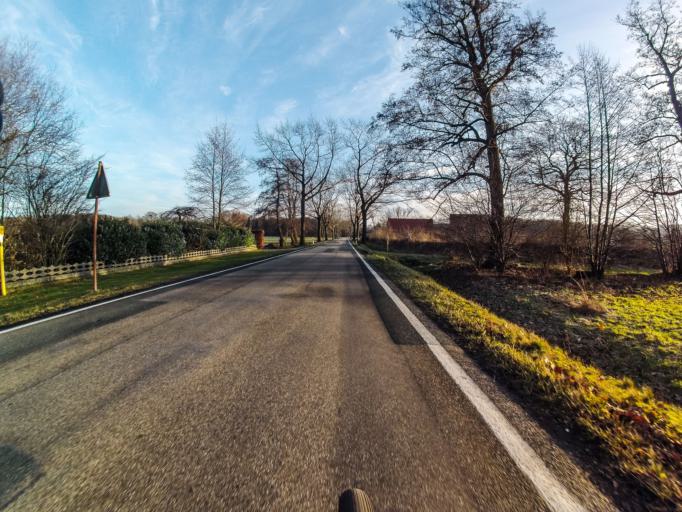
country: DE
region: North Rhine-Westphalia
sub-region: Regierungsbezirk Munster
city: Mettingen
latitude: 52.3006
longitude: 7.8187
